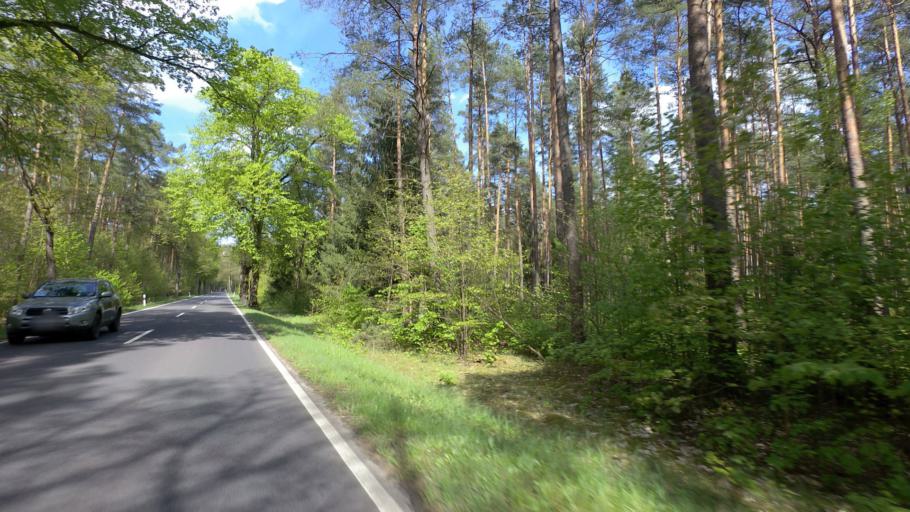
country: DE
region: Brandenburg
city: Milmersdorf
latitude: 53.0166
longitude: 13.6020
